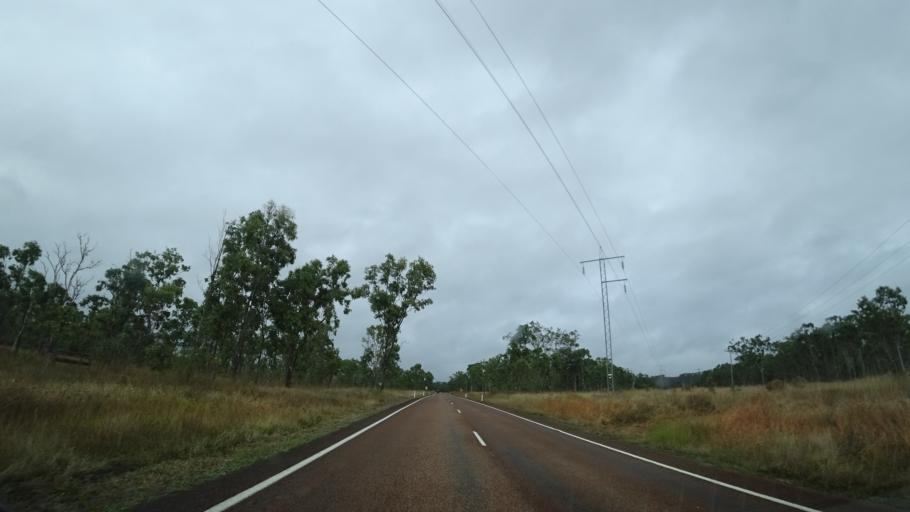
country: AU
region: Queensland
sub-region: Tablelands
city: Ravenshoe
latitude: -17.6725
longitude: 145.2374
